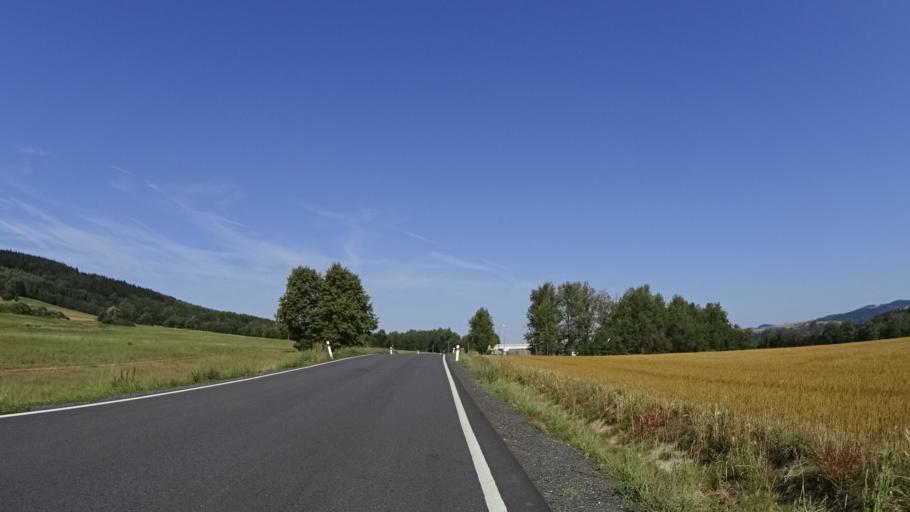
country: CZ
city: Chrastava
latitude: 50.7981
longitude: 14.9863
